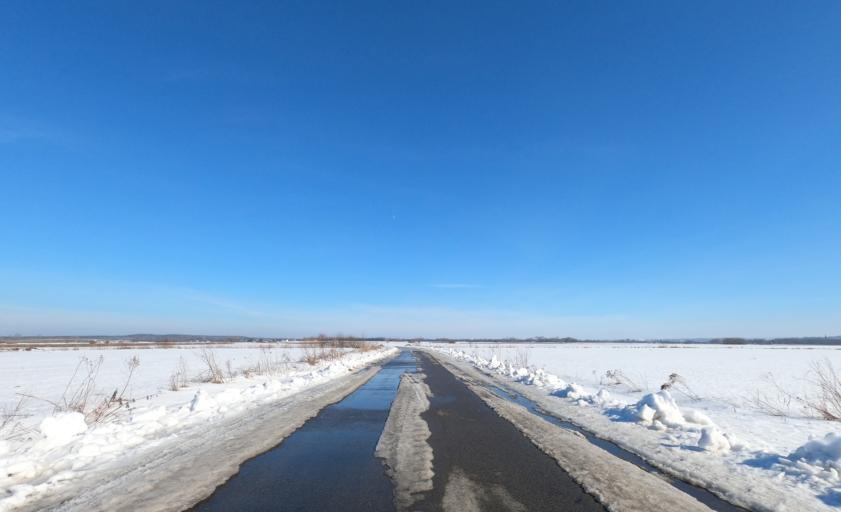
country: PL
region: Subcarpathian Voivodeship
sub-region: Powiat debicki
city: Brzeznica
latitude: 50.0809
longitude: 21.4900
